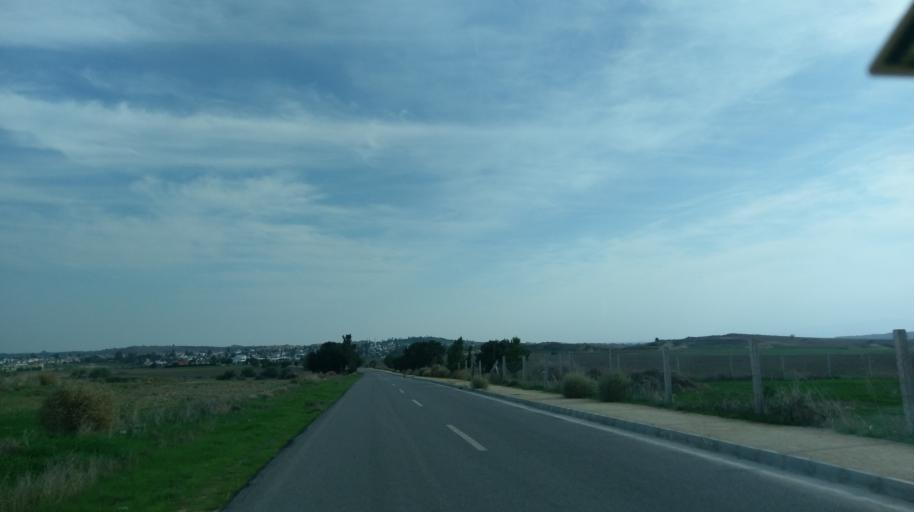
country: CY
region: Lefkosia
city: Mammari
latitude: 35.1915
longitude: 33.2431
